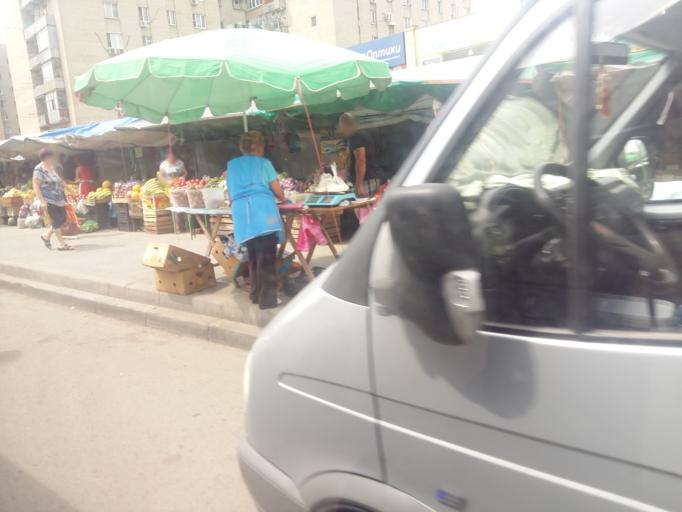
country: RU
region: Rostov
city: Imeni Chkalova
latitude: 47.2848
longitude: 39.7573
